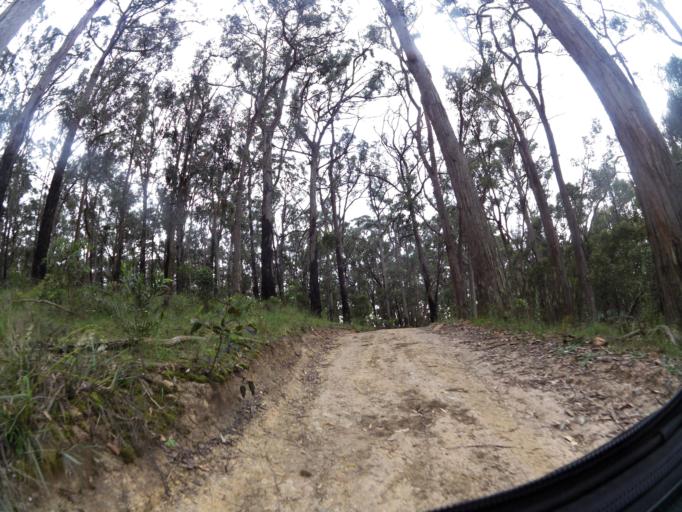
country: AU
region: Victoria
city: Brown Hill
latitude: -37.5166
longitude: 143.9129
